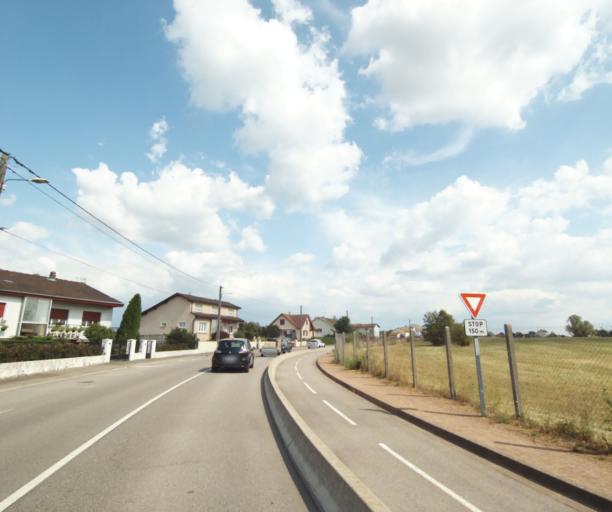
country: FR
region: Lorraine
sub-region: Departement de Meurthe-et-Moselle
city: Chanteheux
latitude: 48.5980
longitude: 6.5172
